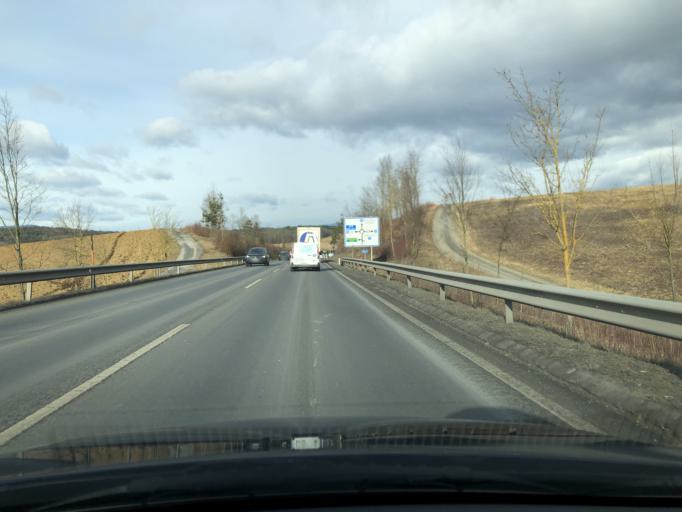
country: AT
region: Burgenland
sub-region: Politischer Bezirk Oberwart
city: Oberwart
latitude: 47.2797
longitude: 16.1918
